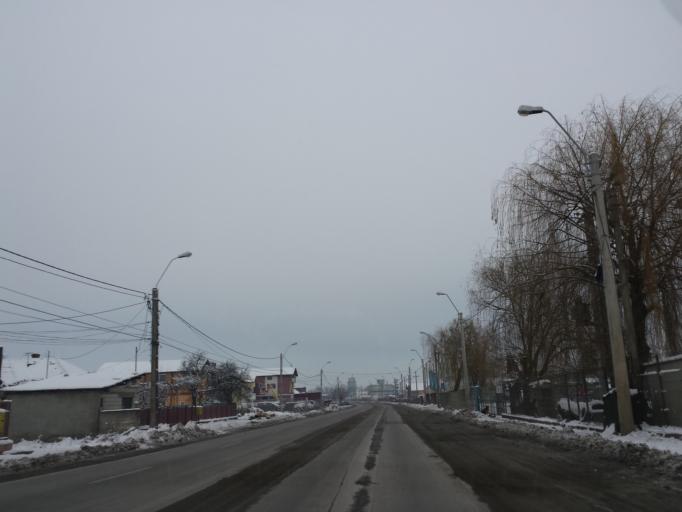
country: RO
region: Hunedoara
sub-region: Municipiul Deva
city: Cristur
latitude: 45.8309
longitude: 22.9464
